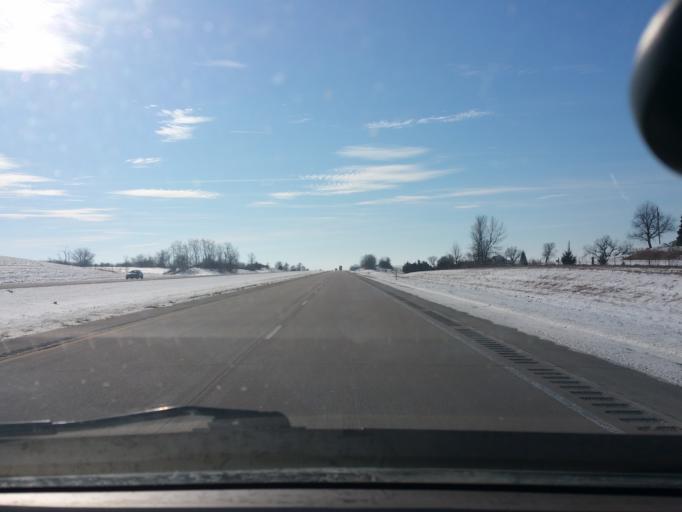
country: US
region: Iowa
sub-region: Decatur County
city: Leon
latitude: 40.8590
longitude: -93.8035
